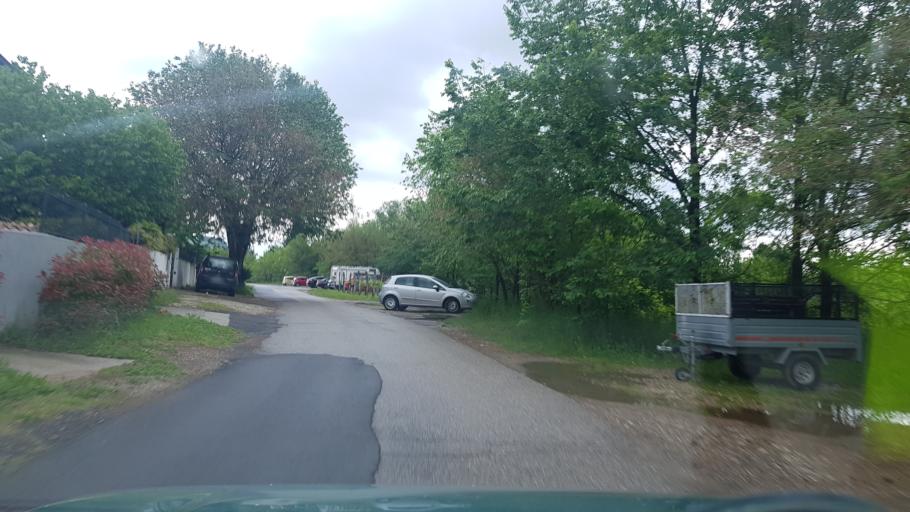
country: IT
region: Friuli Venezia Giulia
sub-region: Provincia di Gorizia
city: Mossa
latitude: 45.9339
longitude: 13.5601
